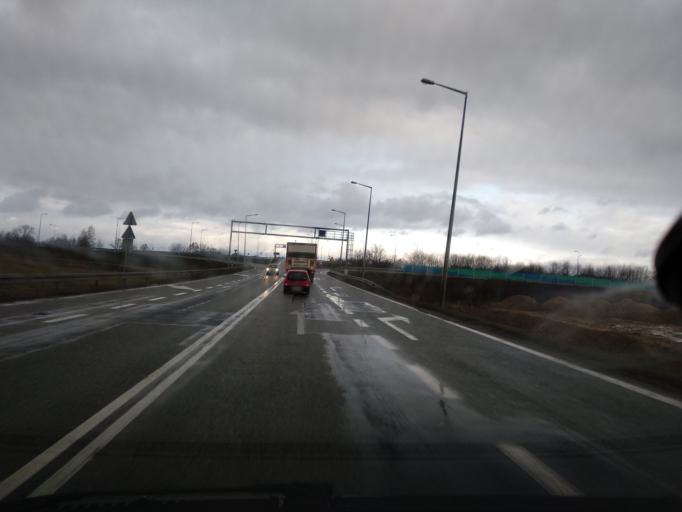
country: PL
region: Greater Poland Voivodeship
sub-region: Powiat koninski
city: Stare Miasto
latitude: 52.1599
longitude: 18.2058
